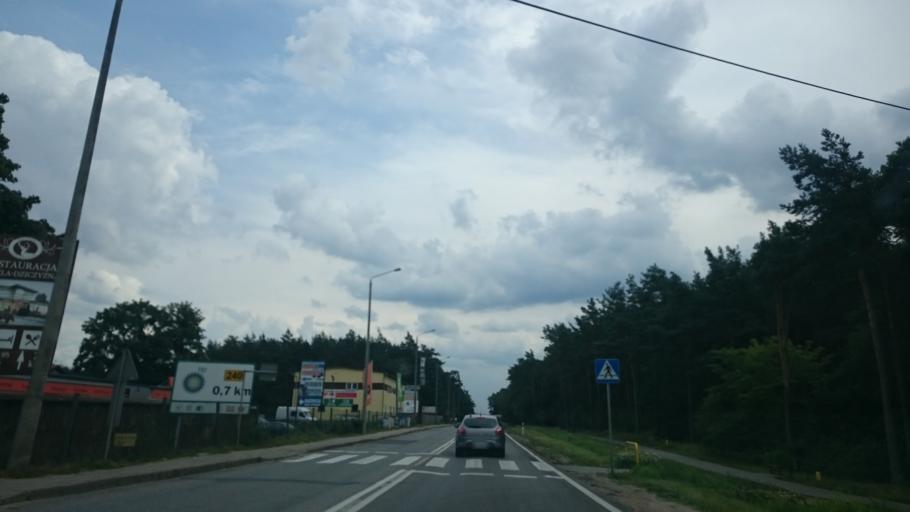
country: PL
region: Kujawsko-Pomorskie
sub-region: Powiat tucholski
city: Tuchola
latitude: 53.5776
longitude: 17.8787
